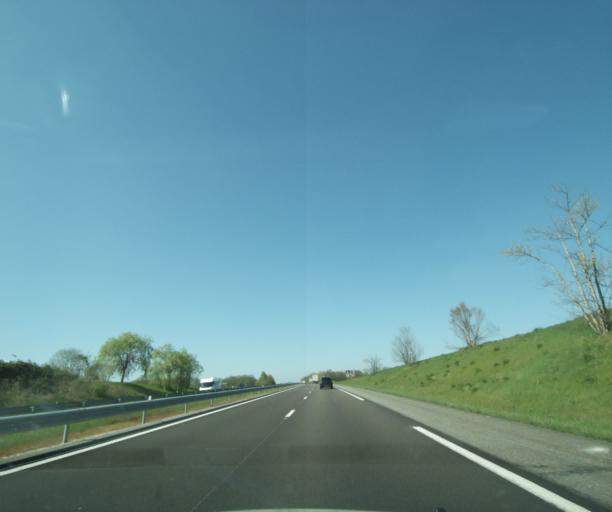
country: FR
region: Bourgogne
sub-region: Departement de la Nievre
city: Neuvy-sur-Loire
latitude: 47.4849
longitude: 2.9413
